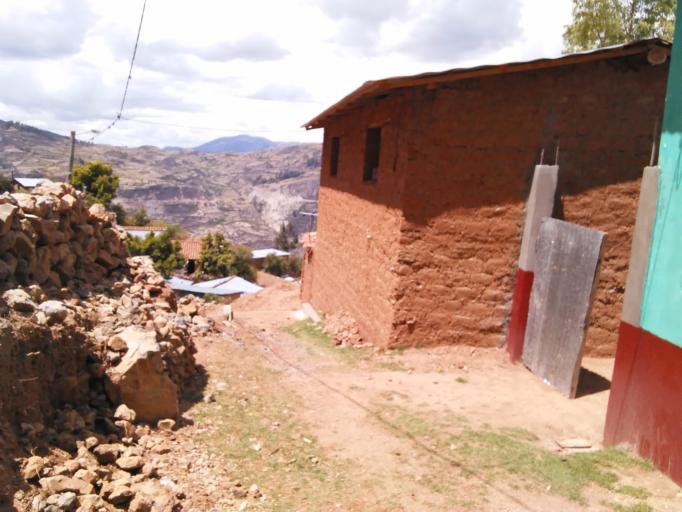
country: PE
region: Ayacucho
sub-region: Provincia de Victor Fajardo
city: Canaria
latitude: -13.8804
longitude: -73.9338
